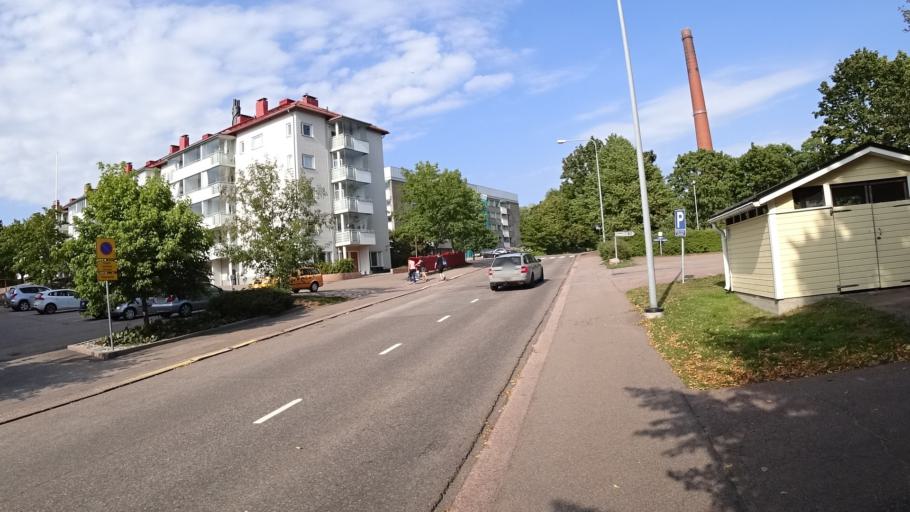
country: FI
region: Kymenlaakso
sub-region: Kotka-Hamina
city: Kotka
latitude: 60.4640
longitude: 26.9524
